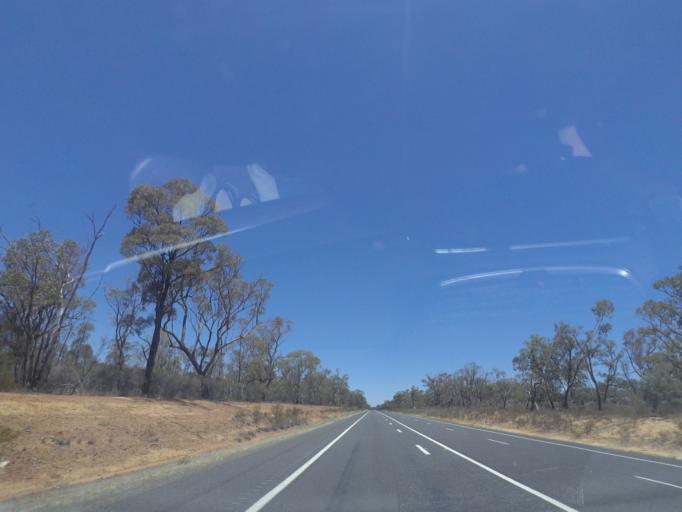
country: AU
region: New South Wales
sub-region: Warrumbungle Shire
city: Coonabarabran
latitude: -30.8717
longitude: 149.4499
